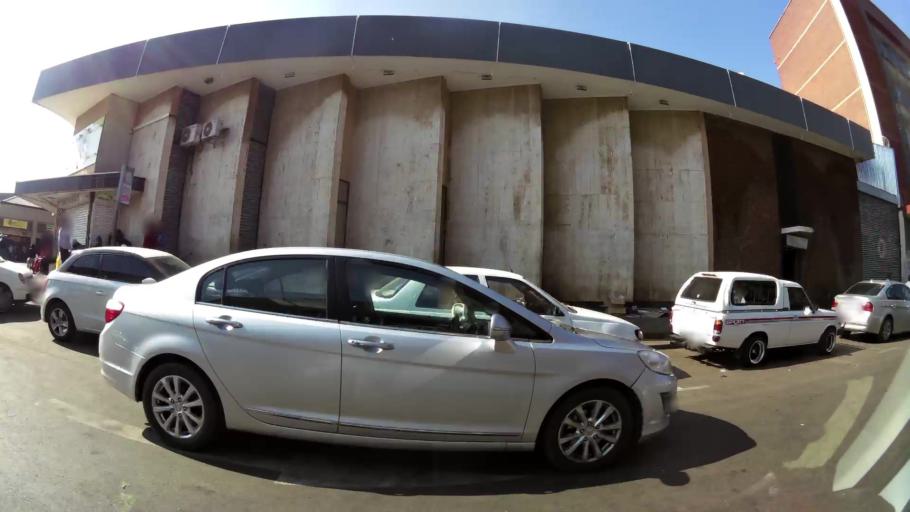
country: ZA
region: Gauteng
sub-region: City of Johannesburg Metropolitan Municipality
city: Modderfontein
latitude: -26.1081
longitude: 28.2299
